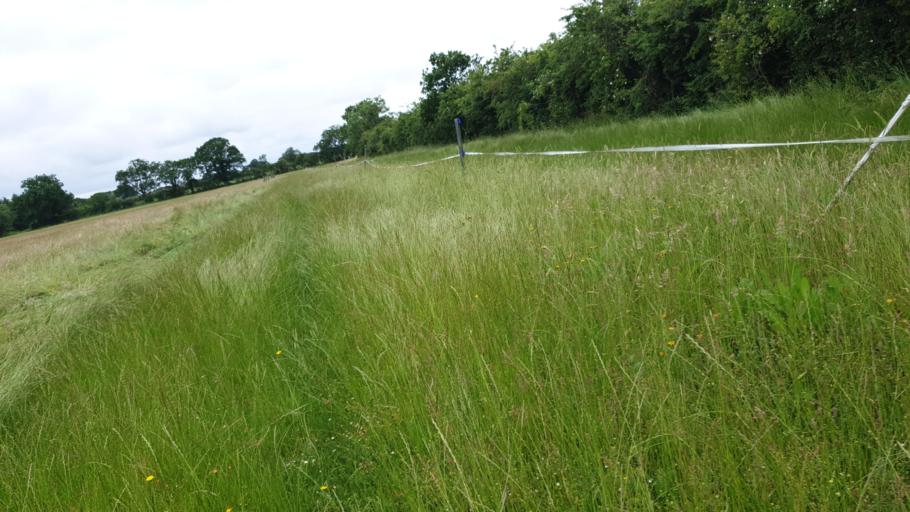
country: GB
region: England
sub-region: Essex
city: Great Bentley
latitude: 51.8860
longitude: 1.0650
